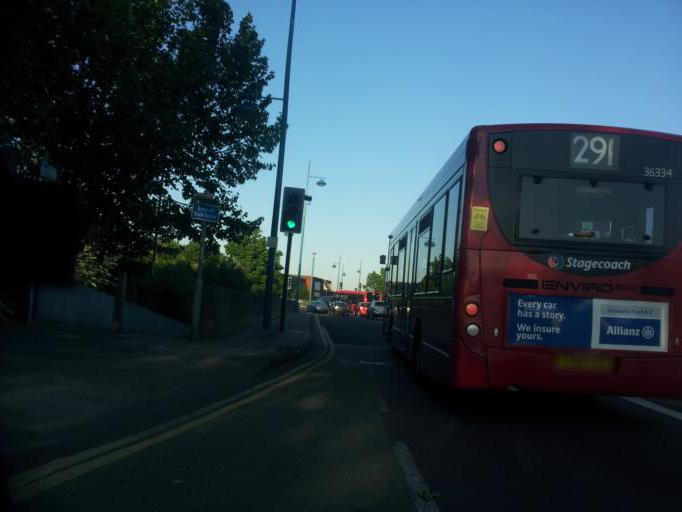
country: GB
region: England
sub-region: Greater London
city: Woolwich
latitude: 51.4911
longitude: 0.0813
